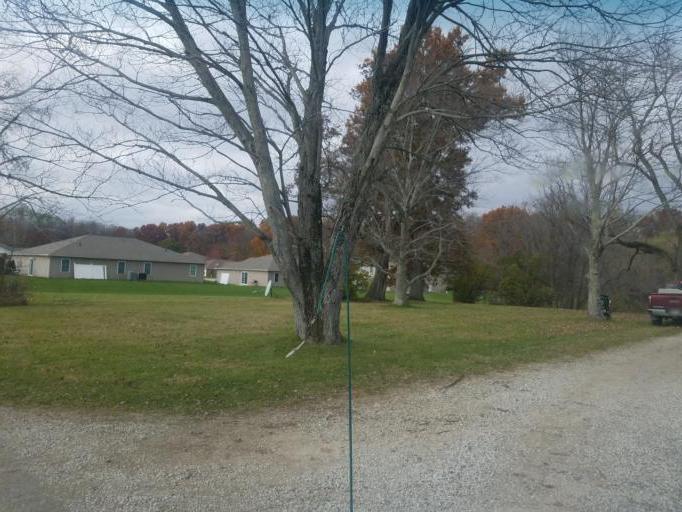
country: US
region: Ohio
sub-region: Richland County
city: Ontario
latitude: 40.7898
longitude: -82.5771
